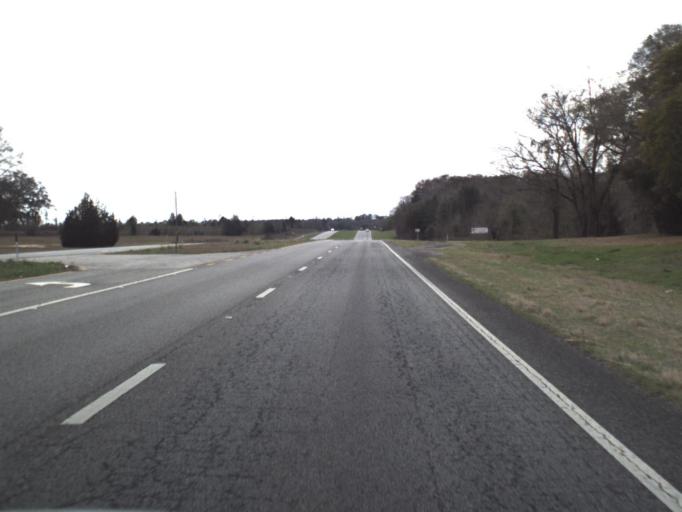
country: US
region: Florida
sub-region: Jackson County
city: Marianna
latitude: 30.8202
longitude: -85.3664
